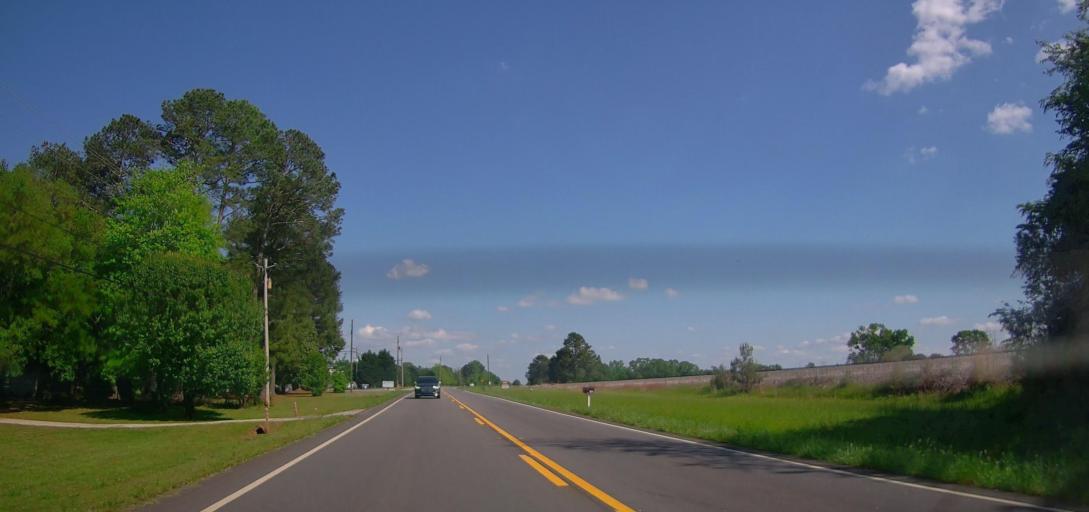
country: US
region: Georgia
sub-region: Morgan County
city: Madison
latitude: 33.6120
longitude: -83.4376
